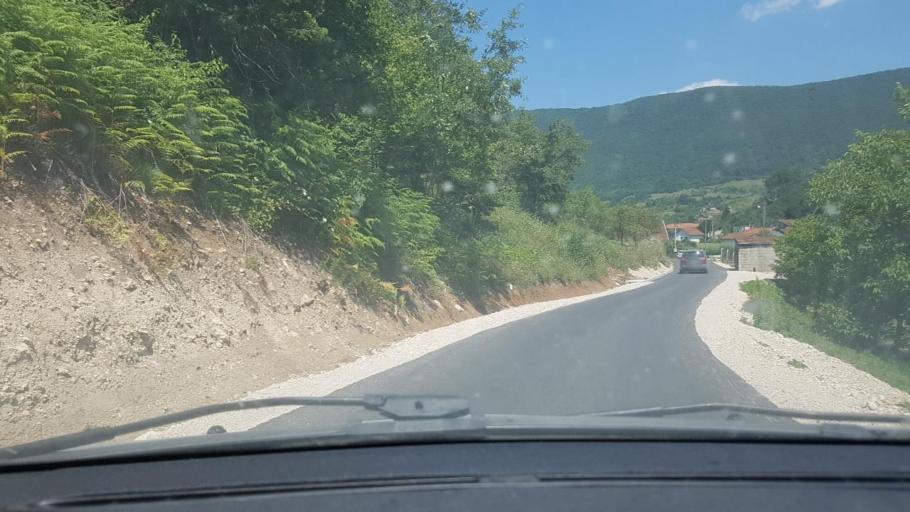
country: BA
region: Federation of Bosnia and Herzegovina
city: Orasac
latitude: 44.6239
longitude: 16.0655
